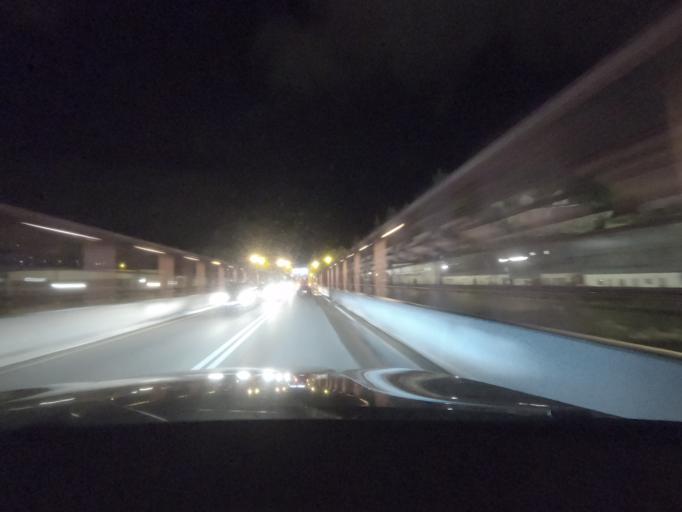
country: PT
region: Vila Real
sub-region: Vila Real
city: Vila Real
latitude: 41.2966
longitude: -7.7405
